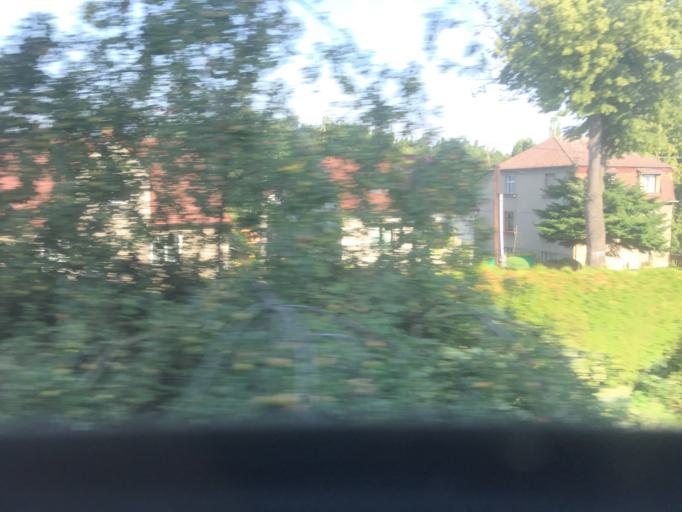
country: CZ
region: Jihocesky
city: Sobeslav
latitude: 49.2999
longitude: 14.7179
